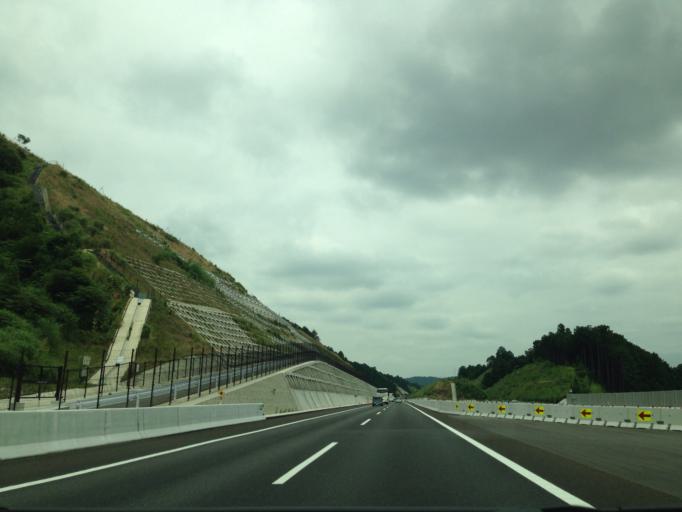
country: JP
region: Aichi
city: Gamagori
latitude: 34.9033
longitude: 137.3103
